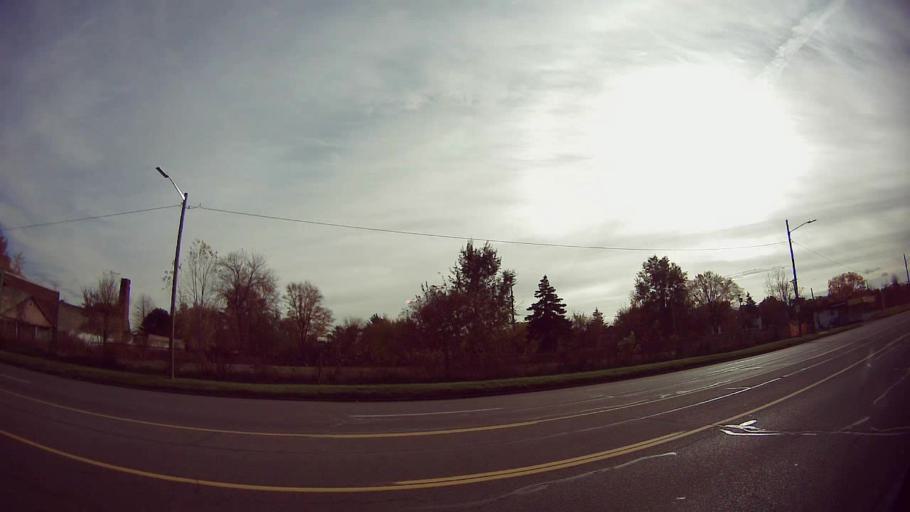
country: US
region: Michigan
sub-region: Wayne County
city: Hamtramck
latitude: 42.4100
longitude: -83.0234
